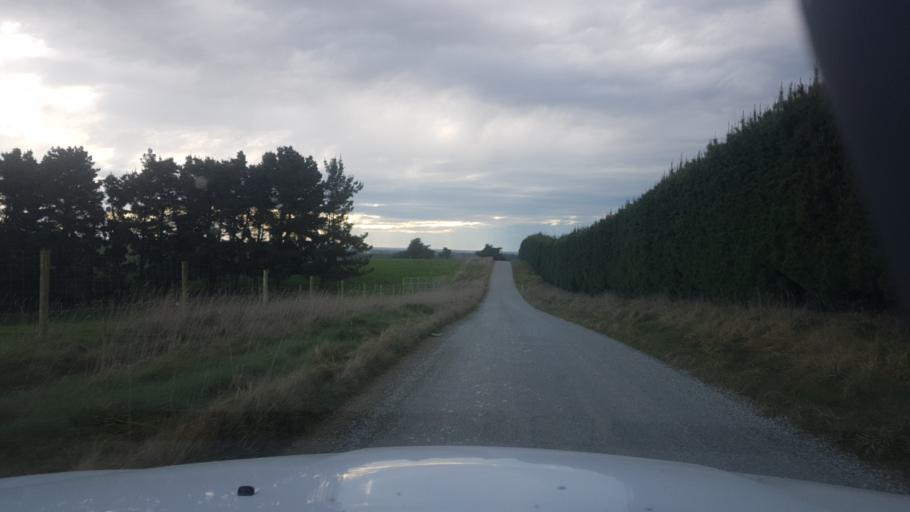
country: NZ
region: Canterbury
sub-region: Timaru District
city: Pleasant Point
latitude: -44.3409
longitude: 171.1431
